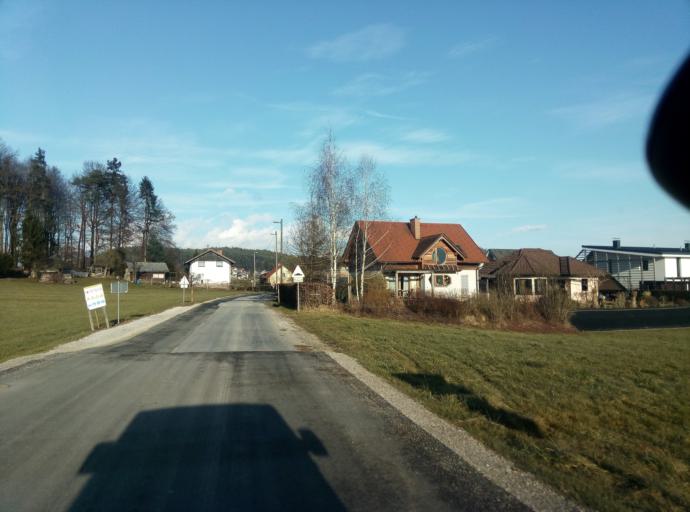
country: SI
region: Vodice
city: Vodice
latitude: 46.1677
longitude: 14.5001
